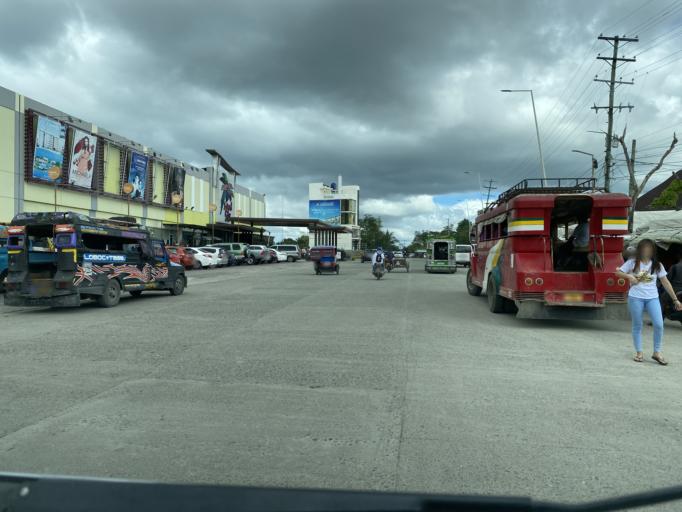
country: PH
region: Central Visayas
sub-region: Province of Bohol
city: Tagbilaran City
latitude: 9.6553
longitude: 123.8704
